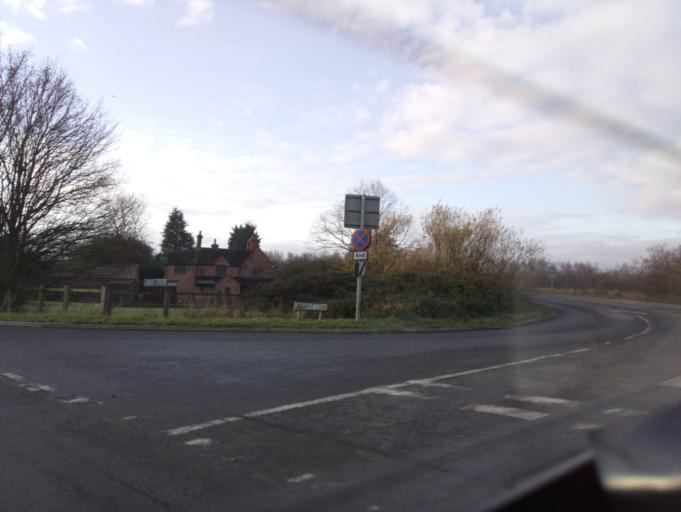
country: GB
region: England
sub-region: Warwickshire
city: Curdworth
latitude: 52.5573
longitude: -1.7434
